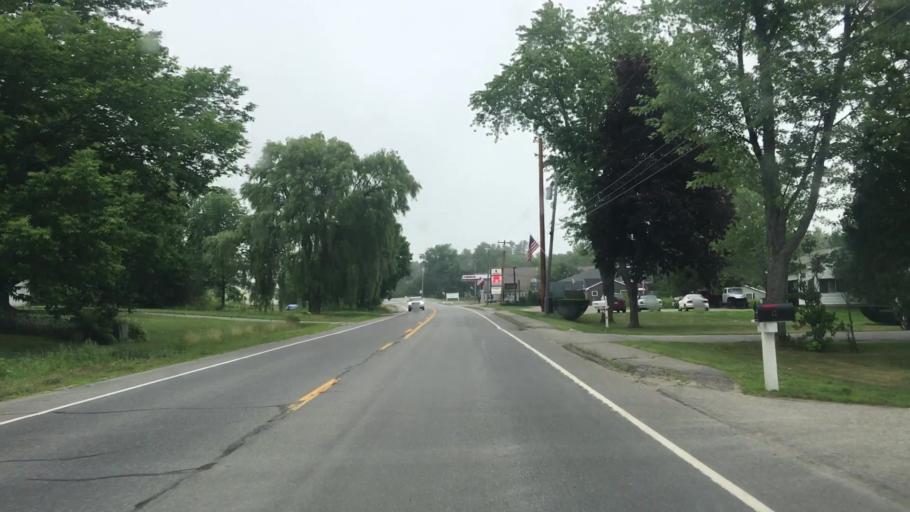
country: US
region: Maine
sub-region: Lincoln County
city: Wiscasset
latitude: 44.0083
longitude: -69.6686
